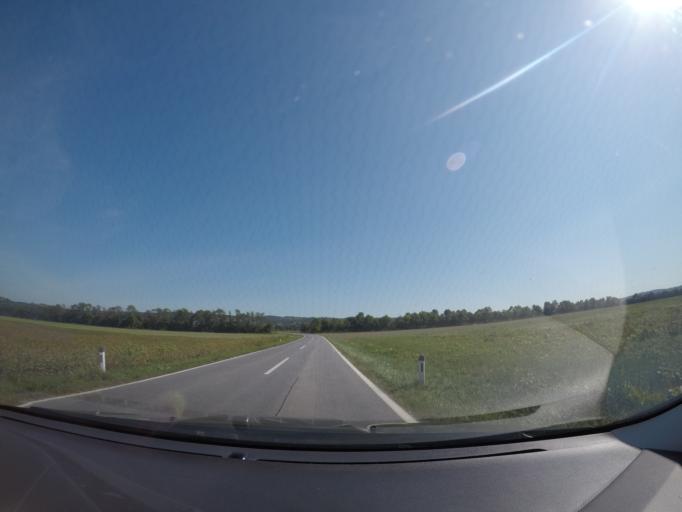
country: AT
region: Lower Austria
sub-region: Politischer Bezirk Bruck an der Leitha
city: Au am Leithaberge
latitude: 47.9464
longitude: 16.5554
